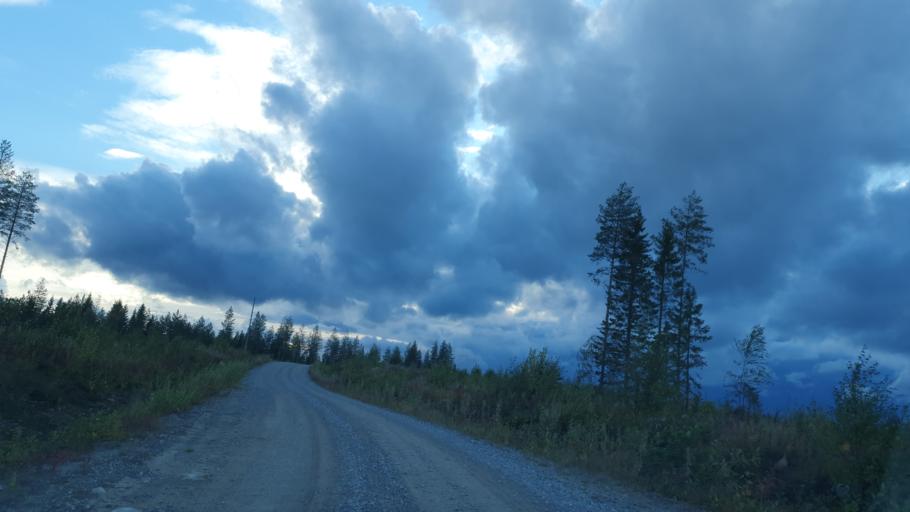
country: FI
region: Kainuu
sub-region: Kehys-Kainuu
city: Kuhmo
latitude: 64.3368
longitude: 29.9074
